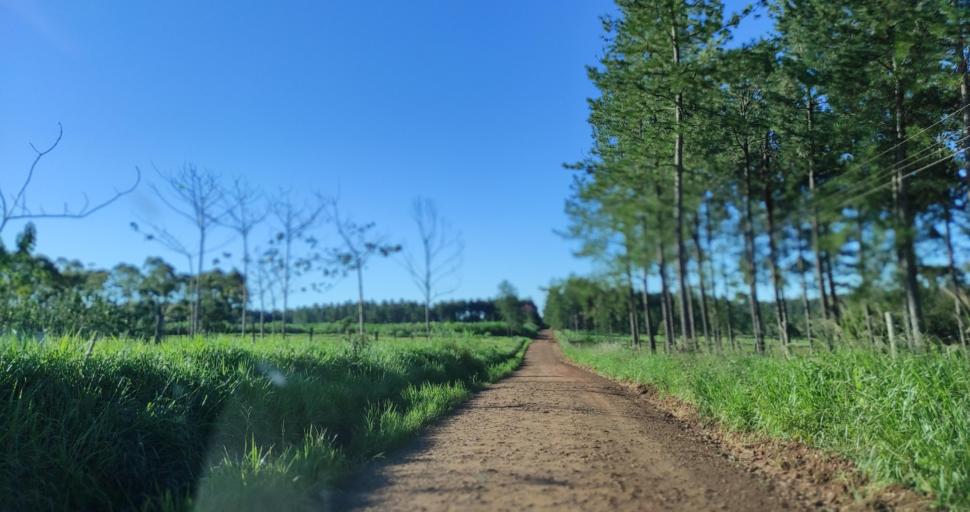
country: AR
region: Misiones
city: Puerto Rico
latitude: -26.8455
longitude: -55.0029
